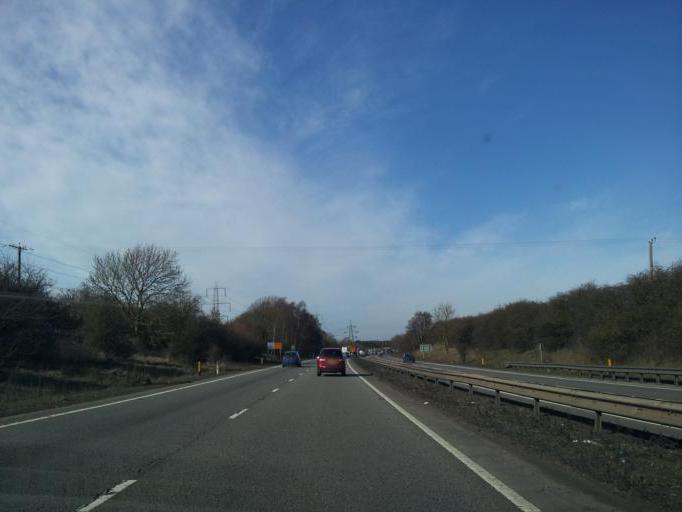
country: GB
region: England
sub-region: Lincolnshire
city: Barrowby
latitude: 52.9120
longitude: -0.6777
